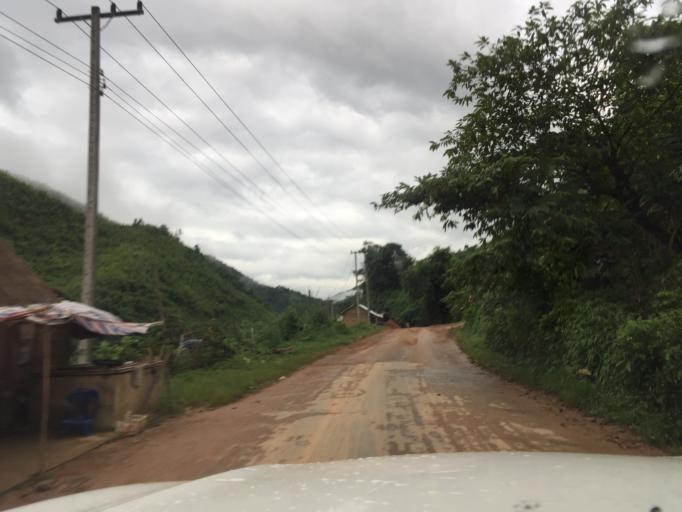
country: LA
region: Oudomxai
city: Muang La
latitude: 20.9591
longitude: 102.2191
